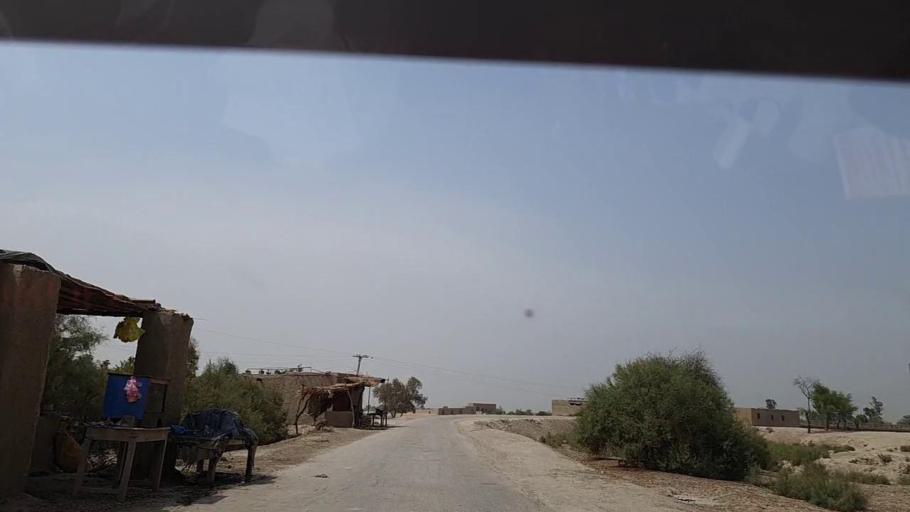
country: PK
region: Sindh
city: Khairpur Nathan Shah
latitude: 27.0735
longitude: 67.6512
